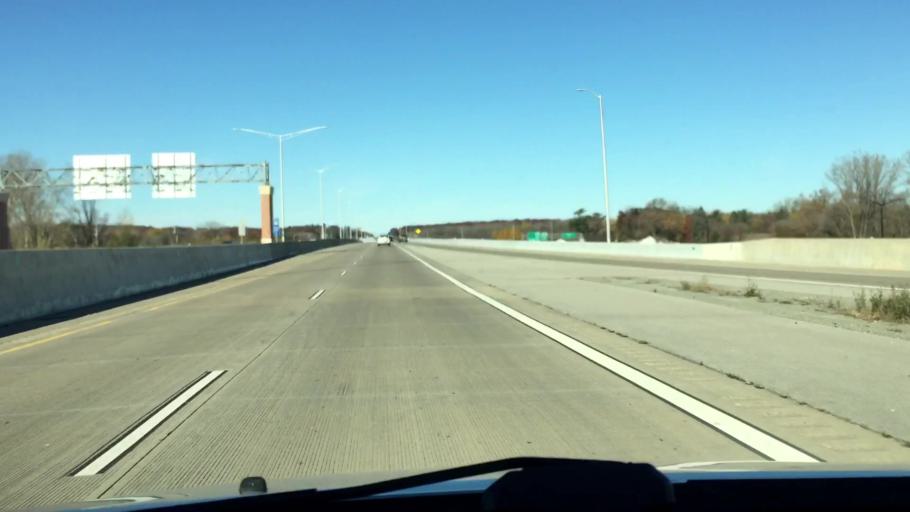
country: US
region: Wisconsin
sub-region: Brown County
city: Howard
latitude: 44.5415
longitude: -88.0840
